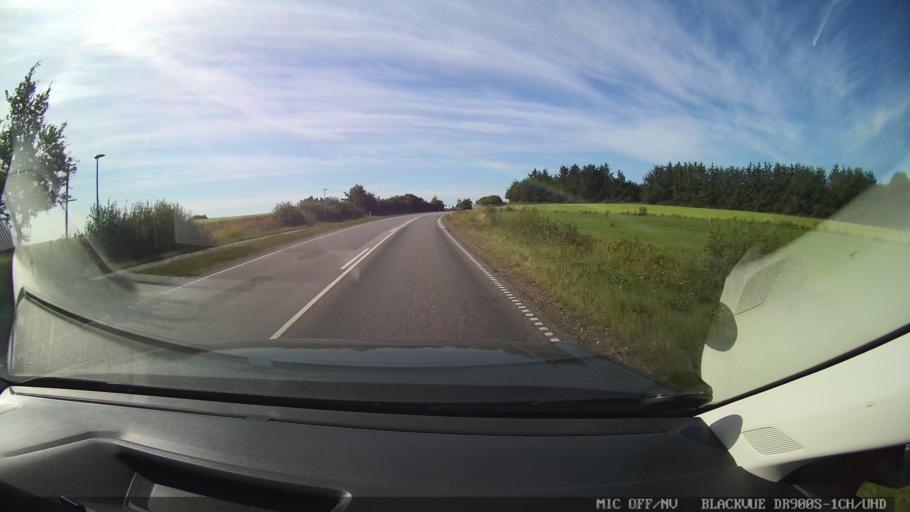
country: DK
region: North Denmark
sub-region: Mariagerfjord Kommune
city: Hobro
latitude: 56.6592
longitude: 9.8231
